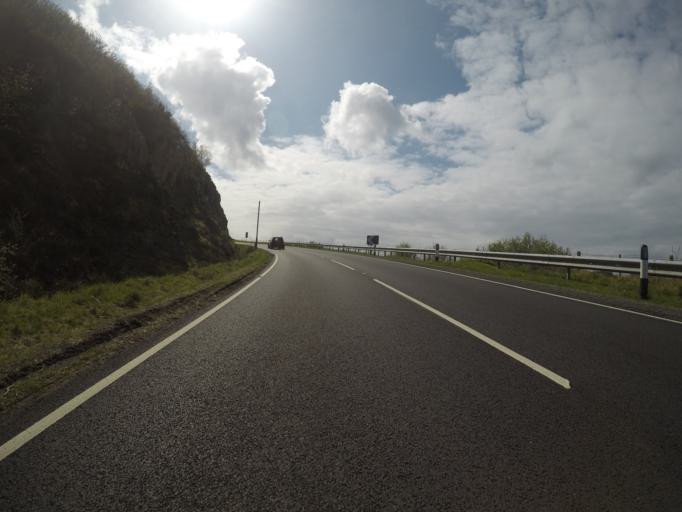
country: GB
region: Scotland
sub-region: Highland
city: Portree
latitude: 57.5806
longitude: -6.3617
